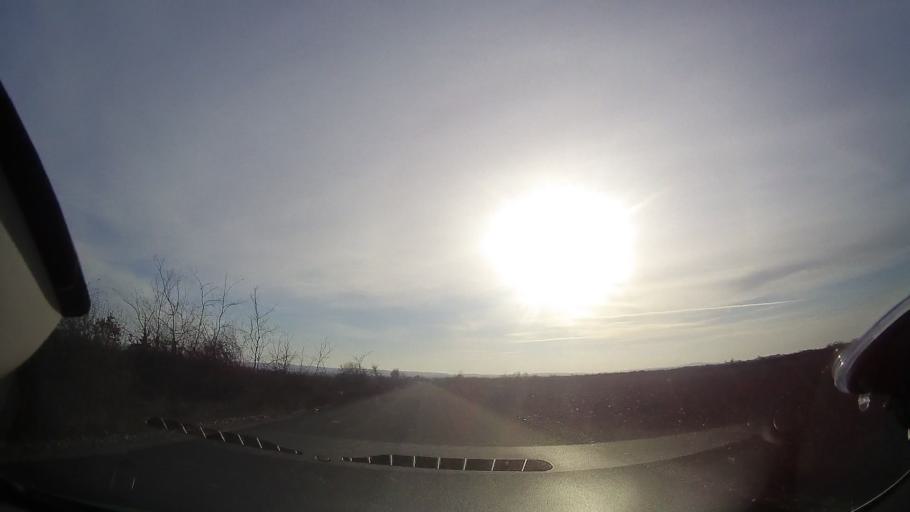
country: RO
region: Bihor
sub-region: Comuna Tileagd
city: Tileagd
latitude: 47.0894
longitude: 22.1773
